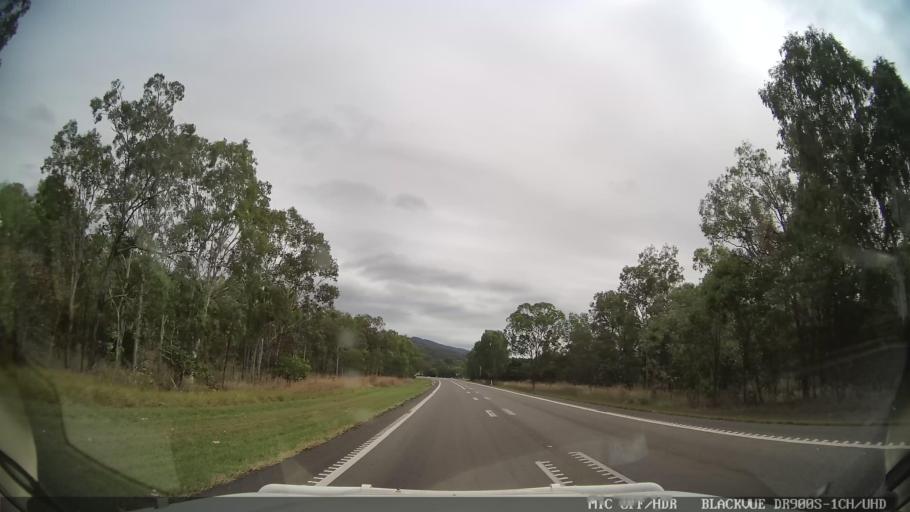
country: AU
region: Queensland
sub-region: Hinchinbrook
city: Ingham
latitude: -18.9538
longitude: 146.2933
